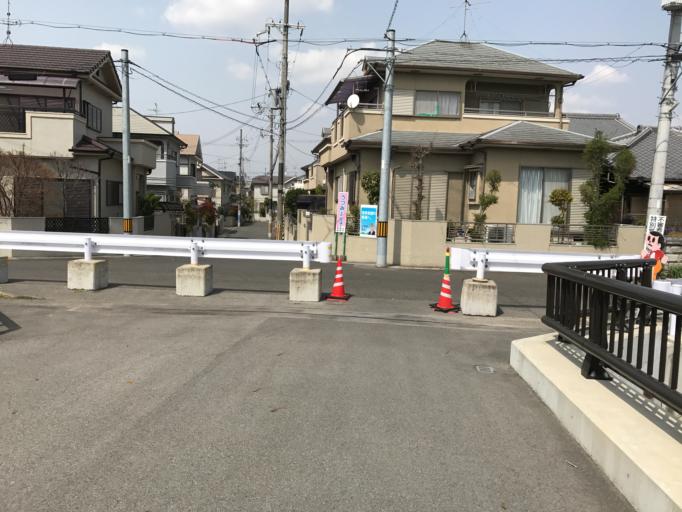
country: JP
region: Kyoto
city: Tanabe
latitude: 34.7809
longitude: 135.7922
